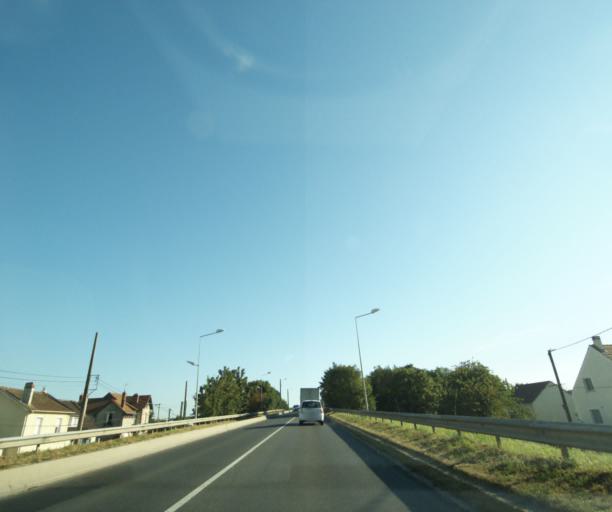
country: FR
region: Ile-de-France
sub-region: Departement de Seine-et-Marne
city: Montereau-Fault-Yonne
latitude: 48.3722
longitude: 2.9577
